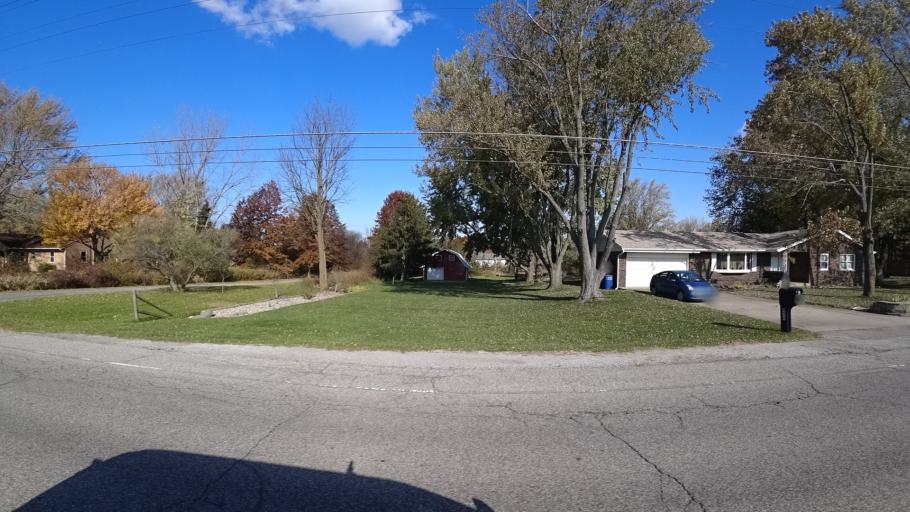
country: US
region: Indiana
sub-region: LaPorte County
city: Trail Creek
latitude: 41.6803
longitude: -86.8637
